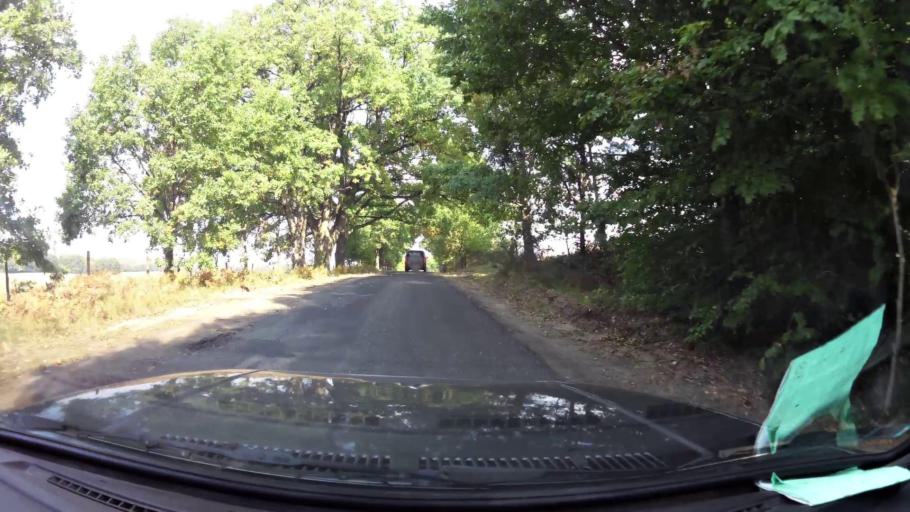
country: PL
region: West Pomeranian Voivodeship
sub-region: Powiat koszalinski
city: Bobolice
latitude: 54.1050
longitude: 16.4984
